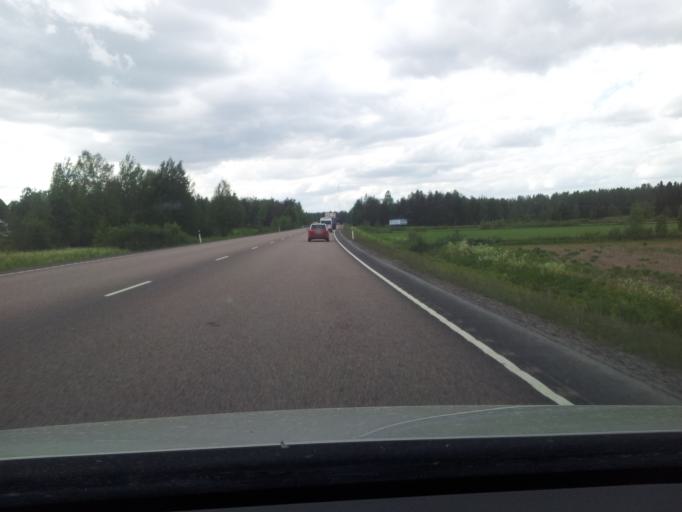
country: FI
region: Kymenlaakso
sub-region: Kotka-Hamina
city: Hamina
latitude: 60.9027
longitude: 27.1466
